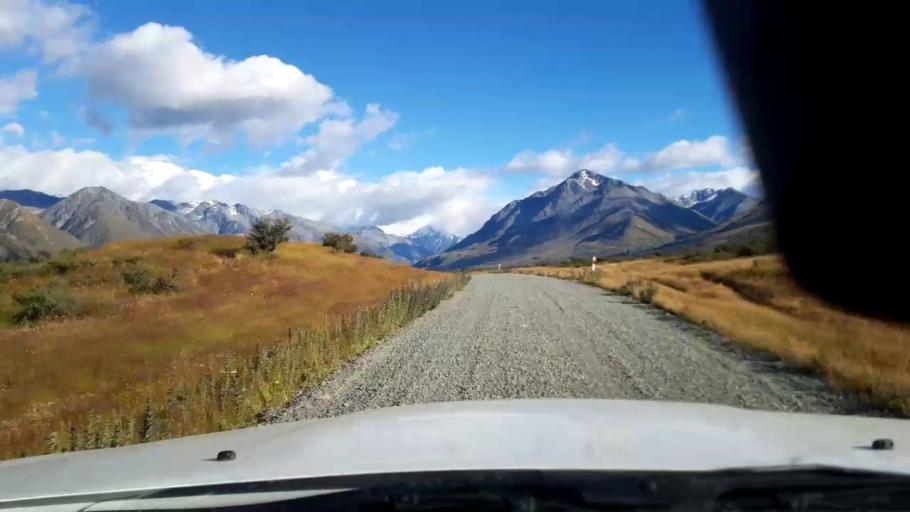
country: NZ
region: Canterbury
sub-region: Timaru District
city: Pleasant Point
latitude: -43.7431
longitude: 170.5718
